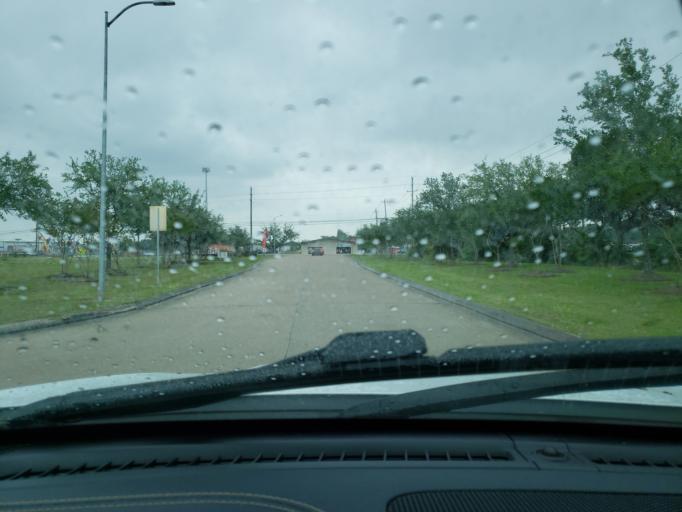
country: US
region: Texas
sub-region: Chambers County
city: Mont Belvieu
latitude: 29.8053
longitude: -94.9049
